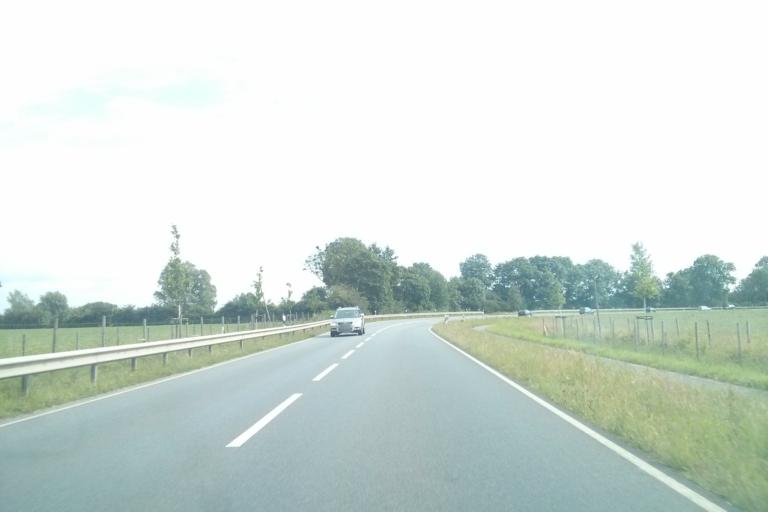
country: DE
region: Lower Saxony
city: Ahsen-Oetzen
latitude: 52.9867
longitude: 9.0538
